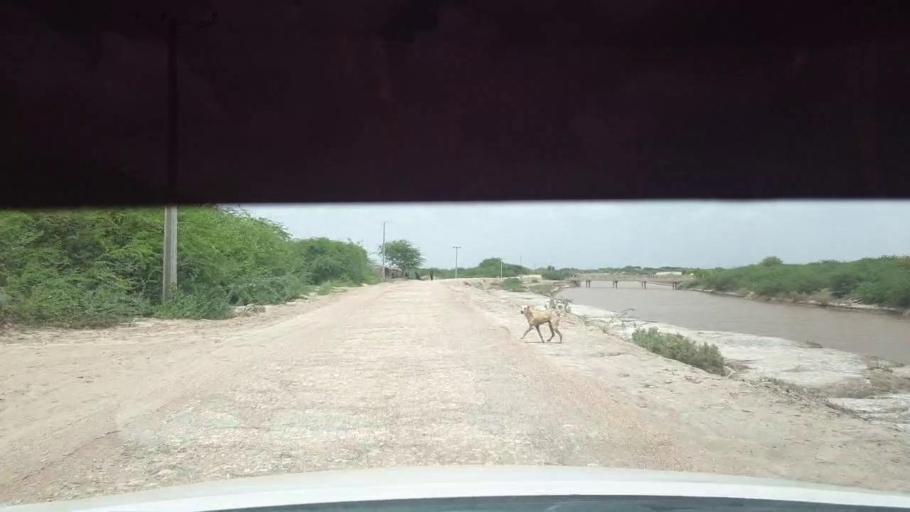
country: PK
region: Sindh
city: Kadhan
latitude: 24.5242
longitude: 69.1229
